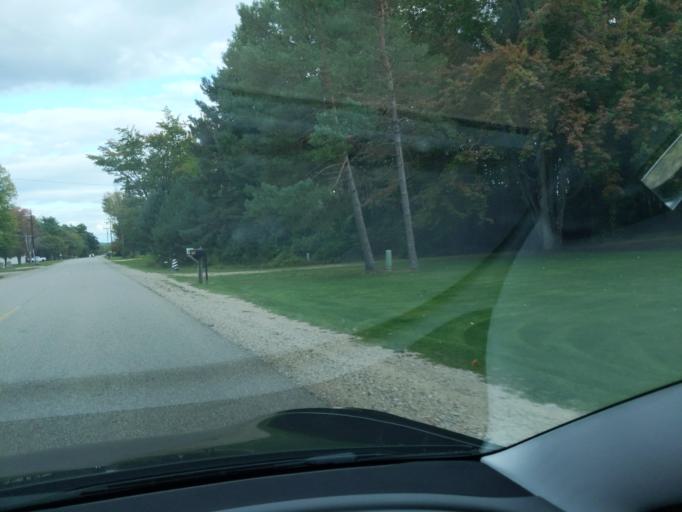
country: US
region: Michigan
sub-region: Kalkaska County
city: Rapid City
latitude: 44.8394
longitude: -85.2964
